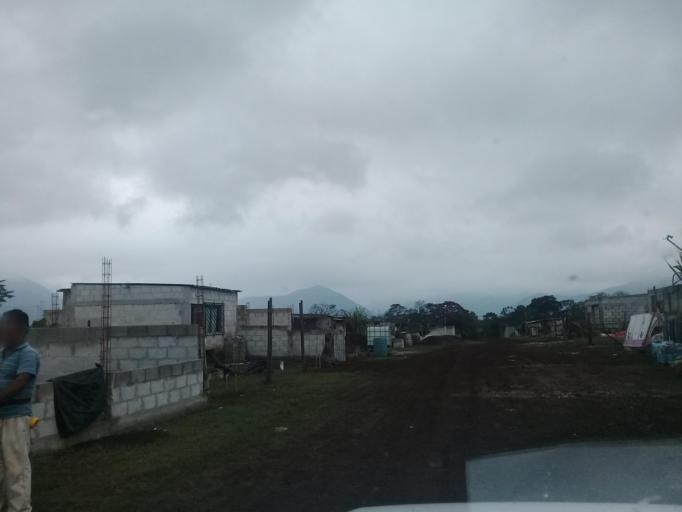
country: MX
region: Veracruz
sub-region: Cordoba
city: San Jose de Tapia
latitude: 18.8555
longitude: -96.9587
